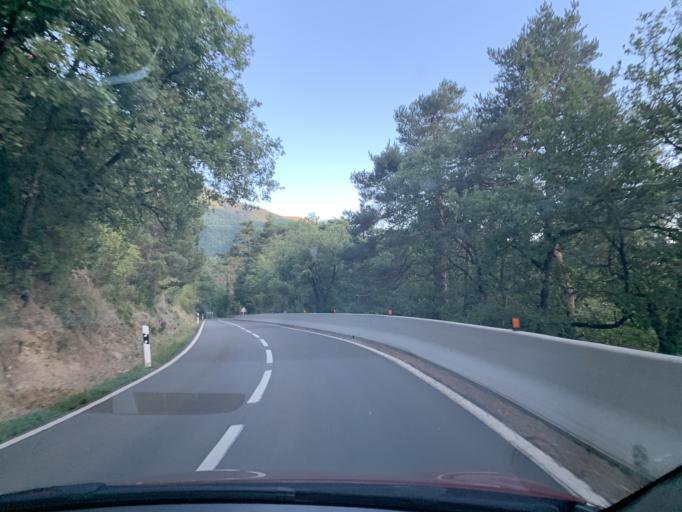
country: ES
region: Aragon
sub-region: Provincia de Huesca
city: Broto
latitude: 42.5821
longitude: -0.1154
